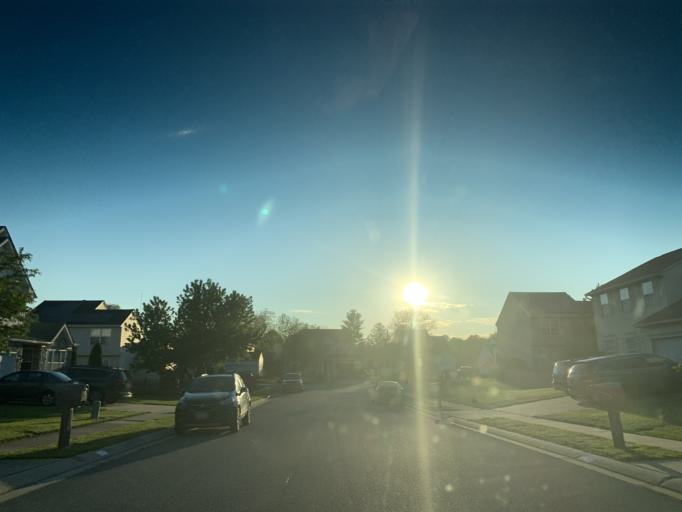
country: US
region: Maryland
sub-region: Harford County
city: Aberdeen
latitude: 39.5120
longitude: -76.1886
